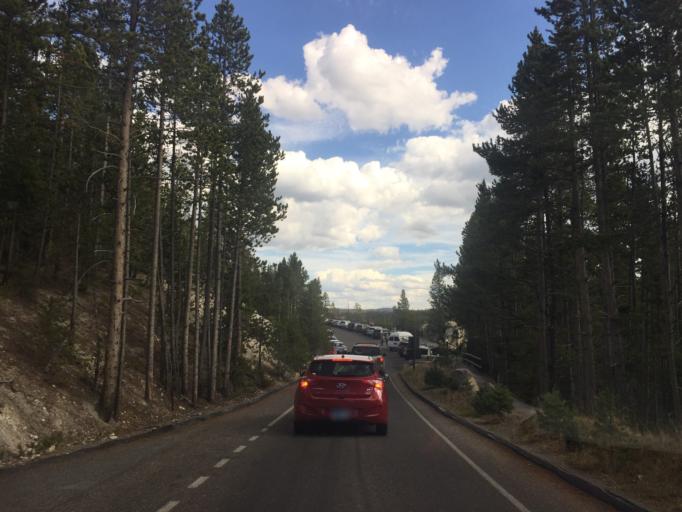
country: US
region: Montana
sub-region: Gallatin County
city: West Yellowstone
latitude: 44.7217
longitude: -110.4889
